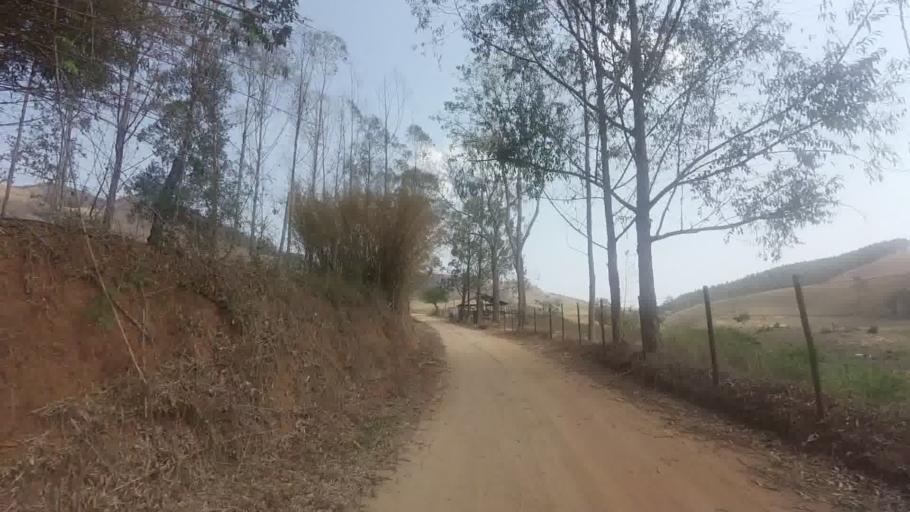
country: BR
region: Espirito Santo
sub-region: Sao Jose Do Calcado
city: Sao Jose do Calcado
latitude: -21.0460
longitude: -41.5229
